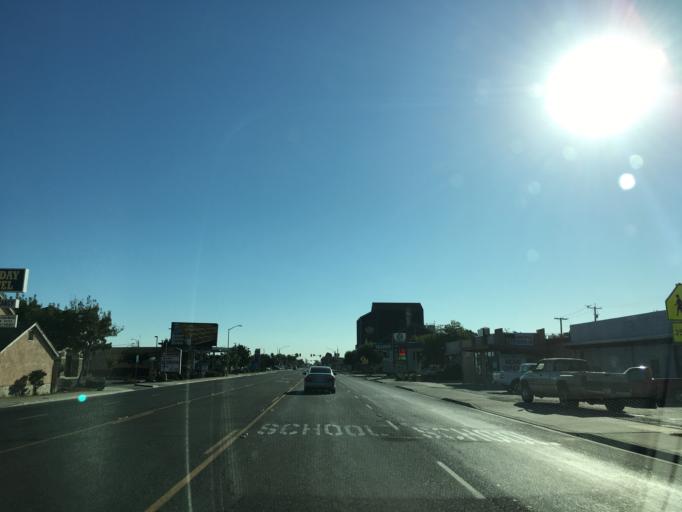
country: US
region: California
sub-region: Merced County
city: Los Banos
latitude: 37.0569
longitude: -120.8420
